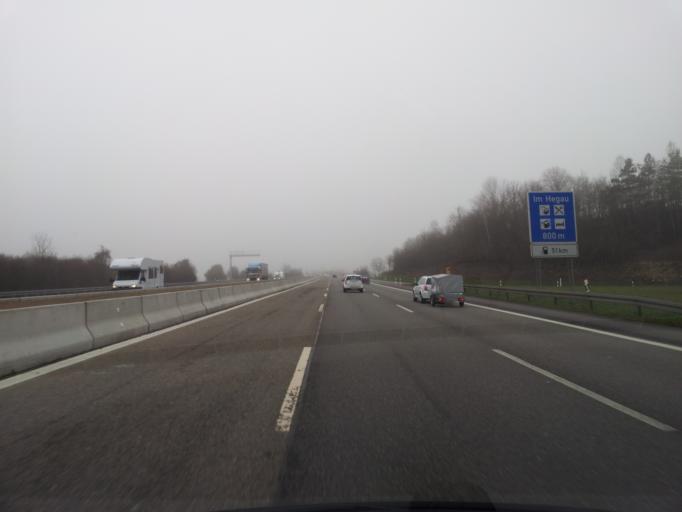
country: DE
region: Baden-Wuerttemberg
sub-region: Freiburg Region
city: Engen
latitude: 47.8549
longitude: 8.7984
